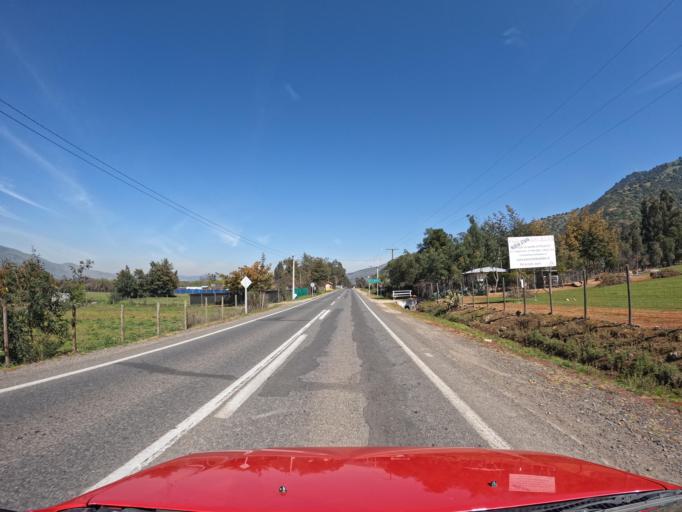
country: CL
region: Maule
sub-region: Provincia de Curico
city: Rauco
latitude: -35.0489
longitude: -71.5983
